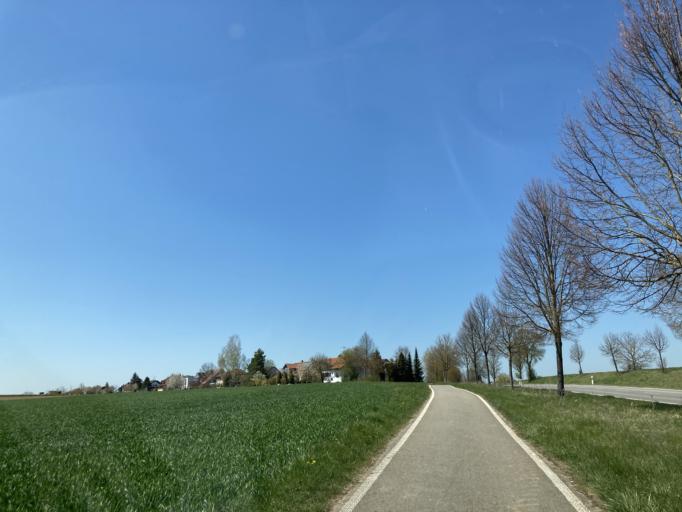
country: DE
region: Baden-Wuerttemberg
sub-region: Regierungsbezirk Stuttgart
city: Bondorf
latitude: 48.5056
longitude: 8.8872
